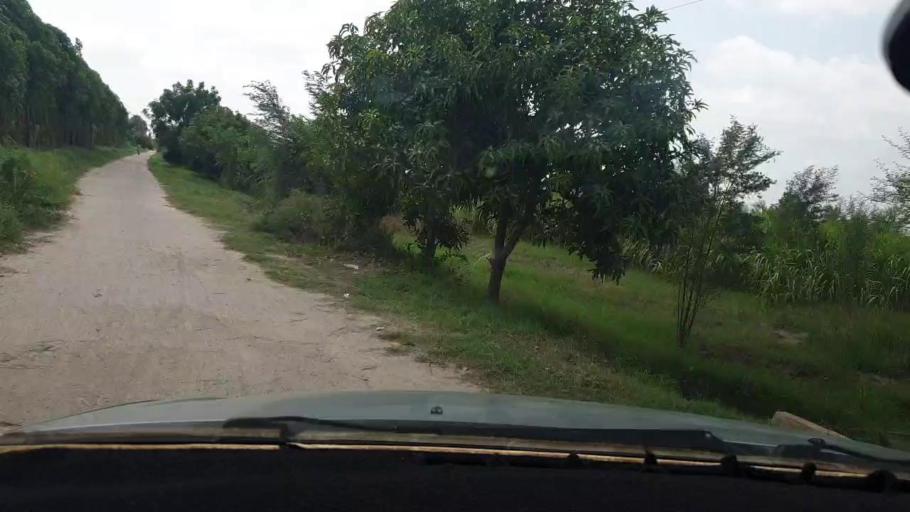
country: PK
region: Sindh
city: Tando Bago
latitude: 24.7553
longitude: 69.1542
